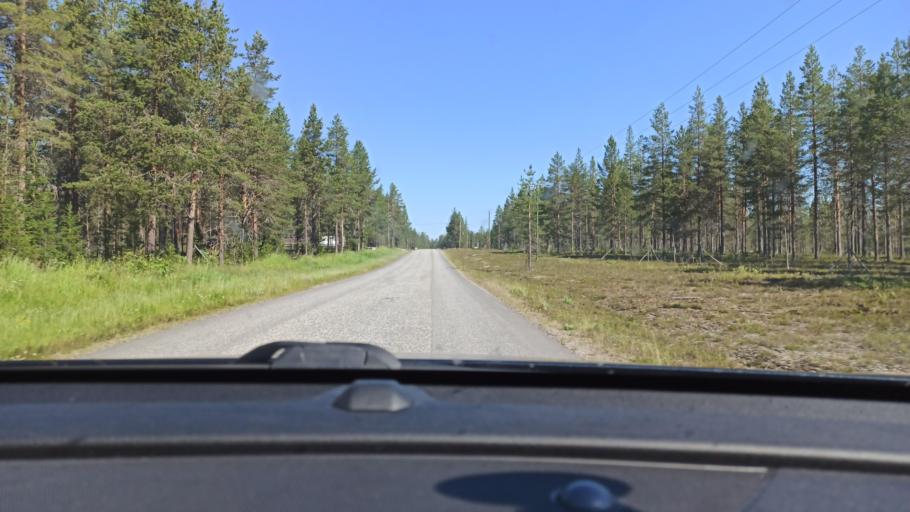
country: FI
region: Lapland
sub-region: Tunturi-Lappi
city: Kolari
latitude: 67.6529
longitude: 24.1630
